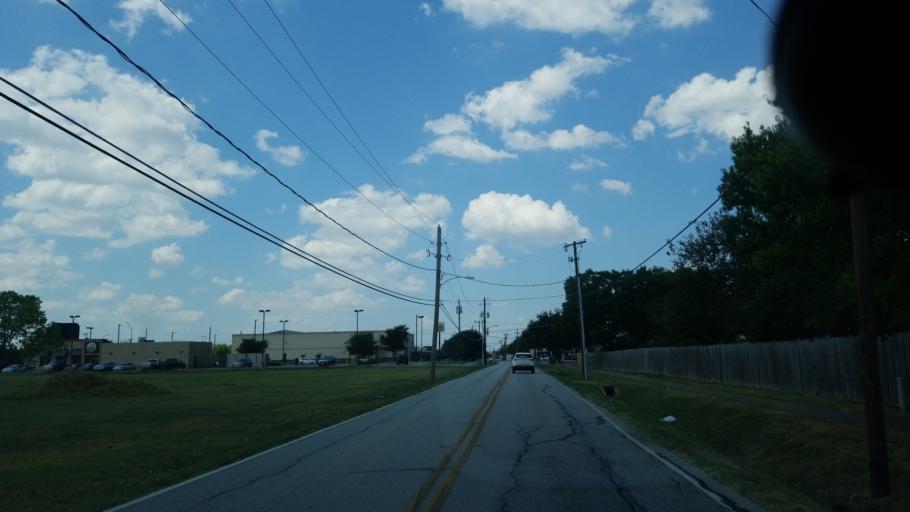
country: US
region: Texas
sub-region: Dallas County
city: Grand Prairie
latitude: 32.7104
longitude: -96.9915
